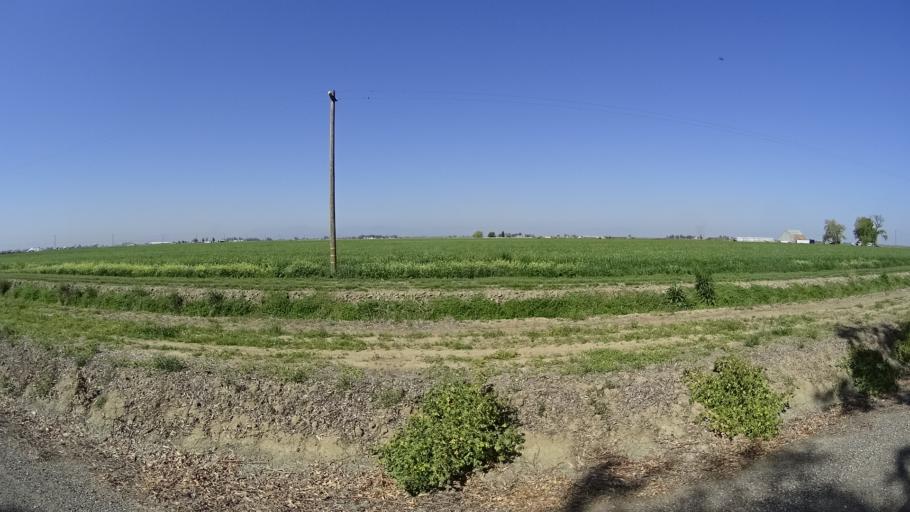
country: US
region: California
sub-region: Glenn County
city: Willows
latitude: 39.5853
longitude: -122.0650
